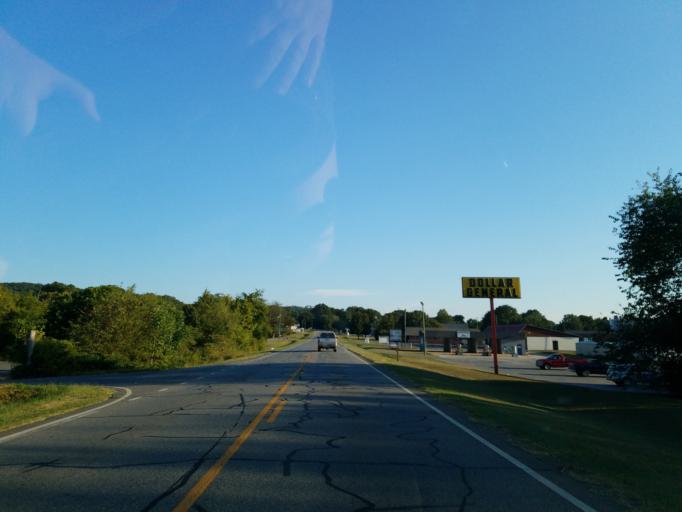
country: US
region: Georgia
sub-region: Bartow County
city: Rydal
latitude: 34.4473
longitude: -84.7022
